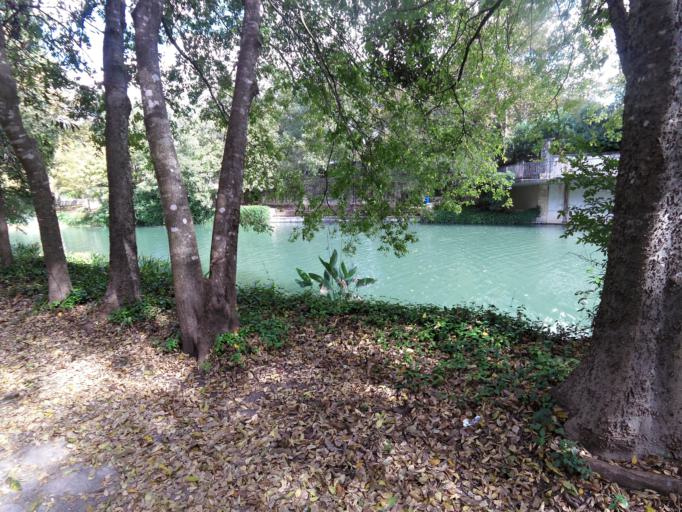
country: US
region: Texas
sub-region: Bexar County
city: San Antonio
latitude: 29.4136
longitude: -98.4954
